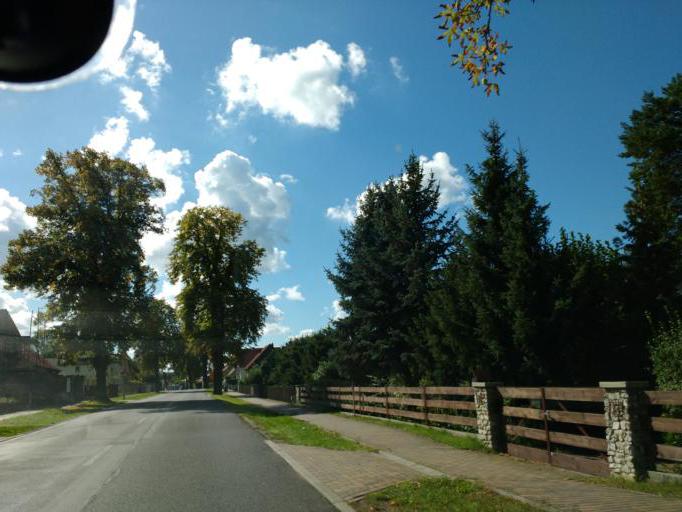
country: DE
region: Brandenburg
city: Mittenwalde
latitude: 52.2083
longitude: 13.5836
